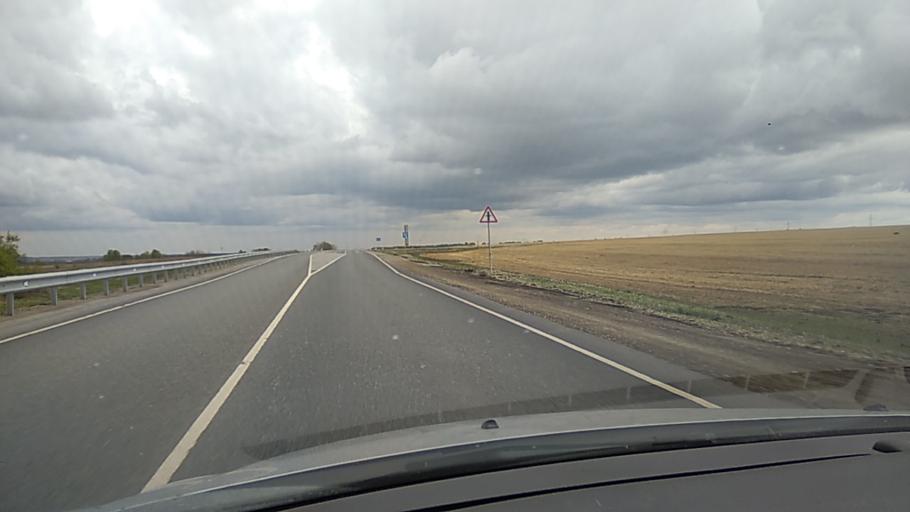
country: RU
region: Kurgan
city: Kataysk
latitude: 56.2878
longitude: 62.7501
